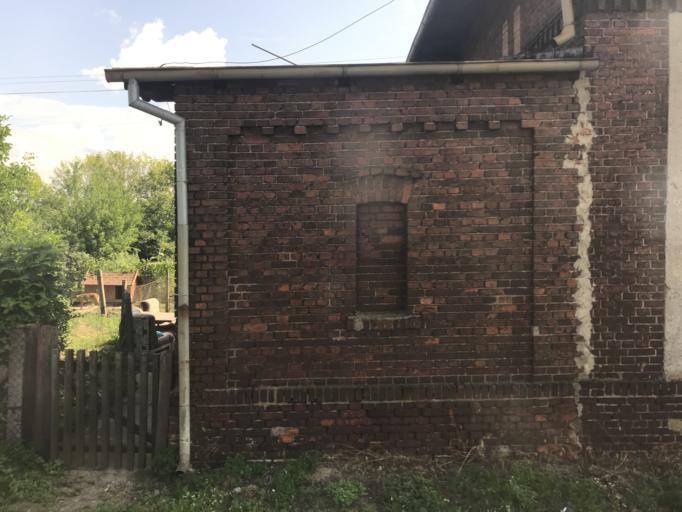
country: PL
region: Kujawsko-Pomorskie
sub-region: Powiat inowroclawski
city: Zlotniki Kujawskie
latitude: 52.9023
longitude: 18.1489
